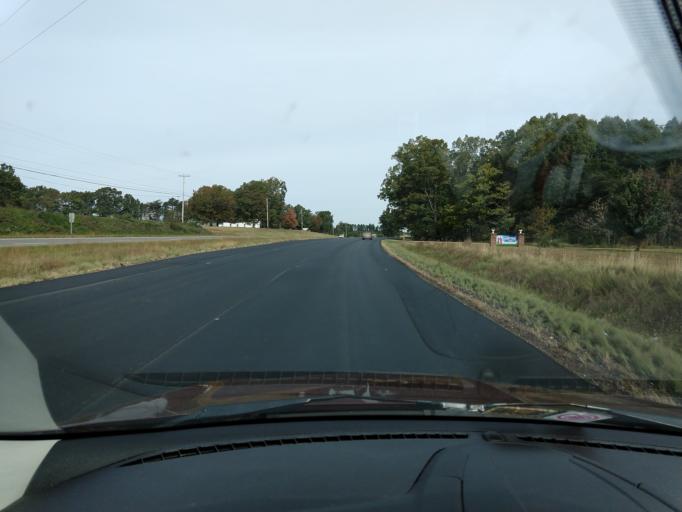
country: US
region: Virginia
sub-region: Pittsylvania County
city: Chatham
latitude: 36.8724
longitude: -79.4091
